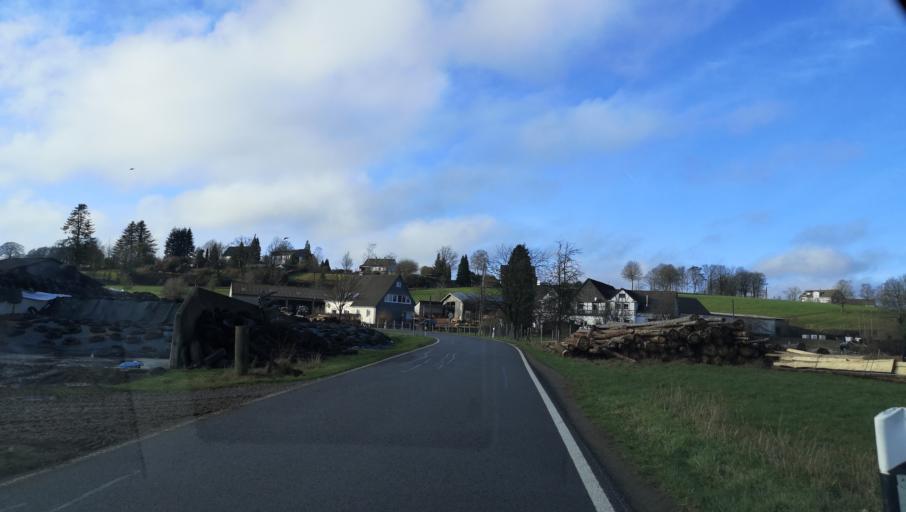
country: DE
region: North Rhine-Westphalia
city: Radevormwald
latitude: 51.1727
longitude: 7.3672
